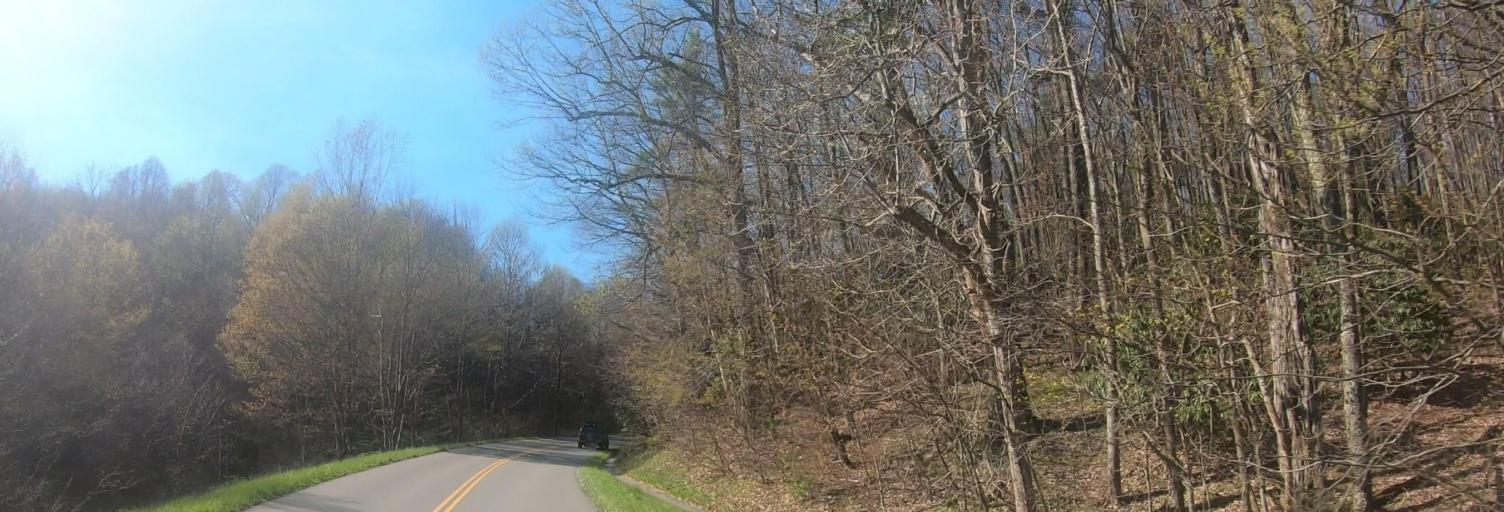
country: US
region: North Carolina
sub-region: Watauga County
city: Boone
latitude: 36.2077
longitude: -81.6029
